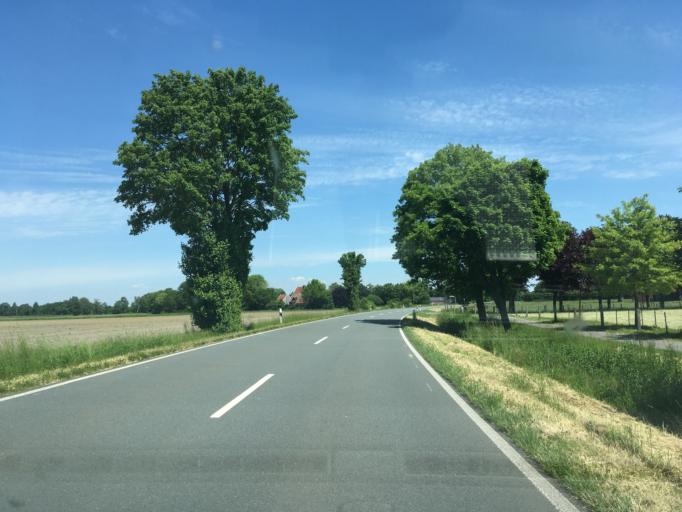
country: DE
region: North Rhine-Westphalia
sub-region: Regierungsbezirk Munster
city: Sudlohn
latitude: 51.8943
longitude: 6.8190
